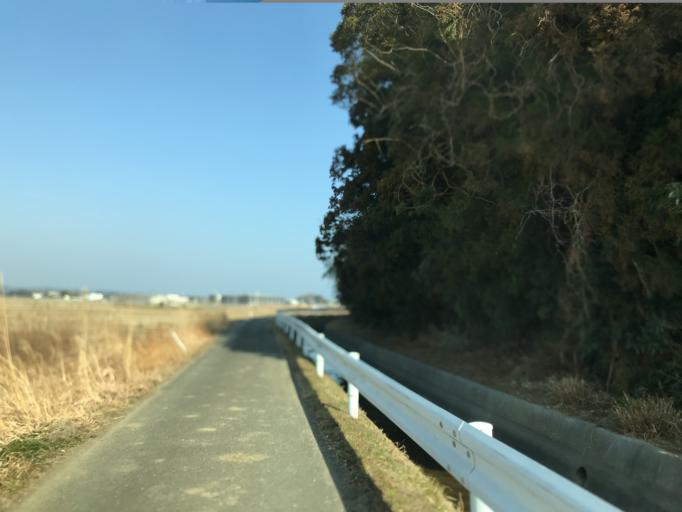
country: JP
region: Fukushima
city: Iwaki
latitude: 37.0484
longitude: 140.9450
